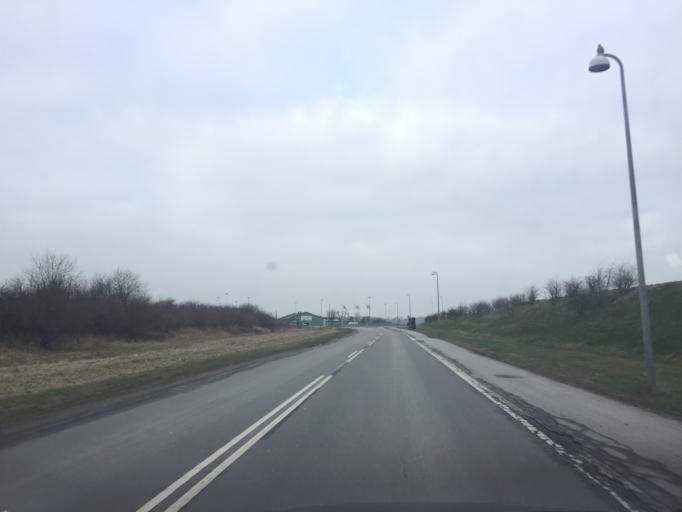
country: DK
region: Zealand
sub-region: Greve Kommune
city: Greve
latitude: 55.5952
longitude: 12.2642
